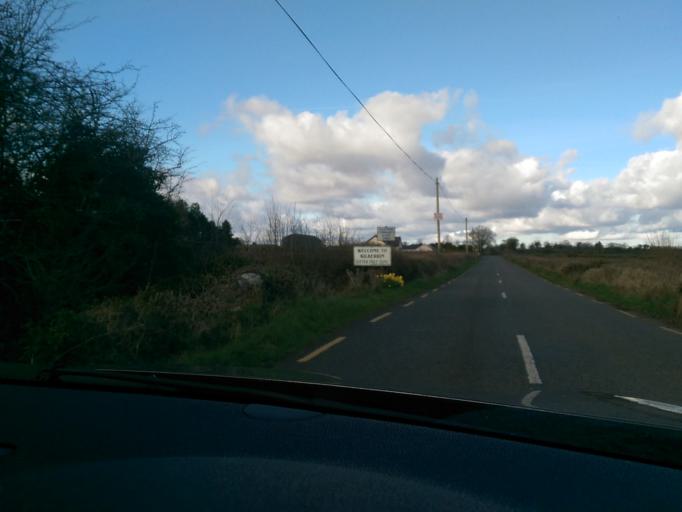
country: IE
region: Connaught
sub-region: Roscommon
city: Castlerea
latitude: 53.5212
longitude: -8.5747
